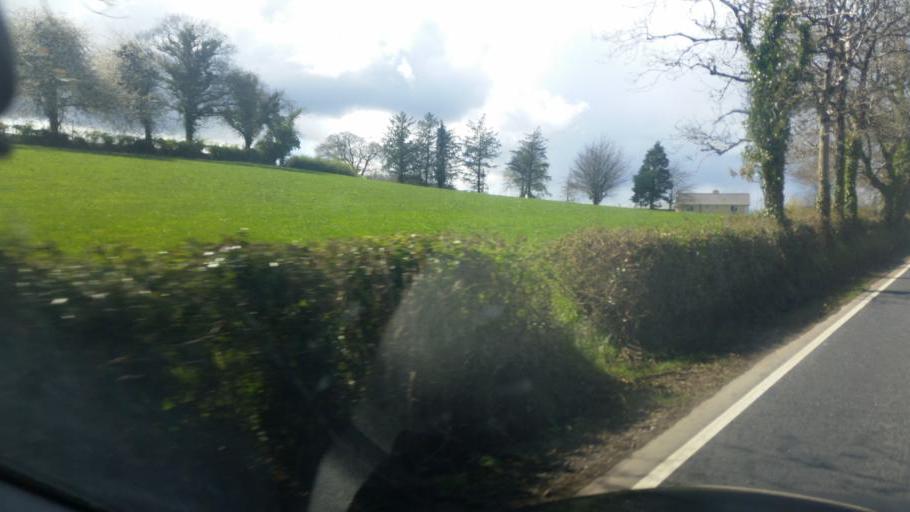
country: GB
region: Northern Ireland
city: Irvinestown
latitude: 54.4276
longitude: -7.7664
